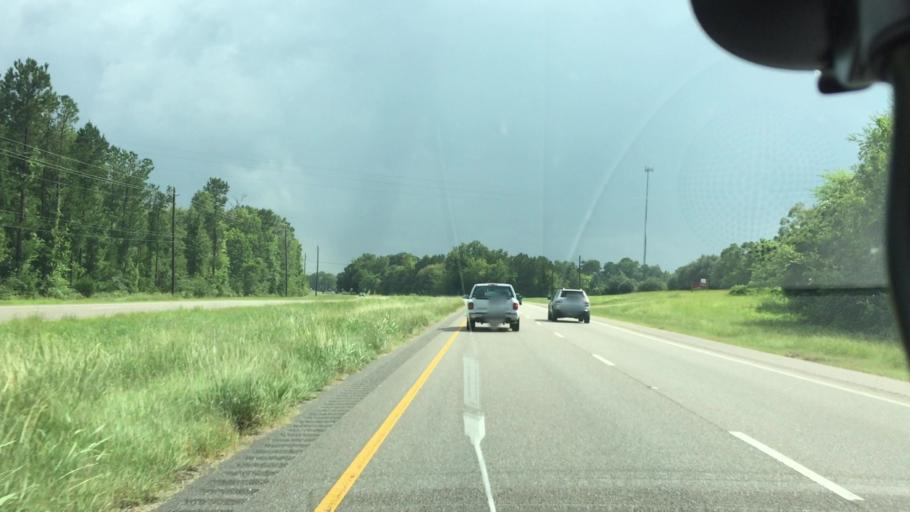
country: US
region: Alabama
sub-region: Montgomery County
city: Pike Road
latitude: 32.3042
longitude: -86.1943
